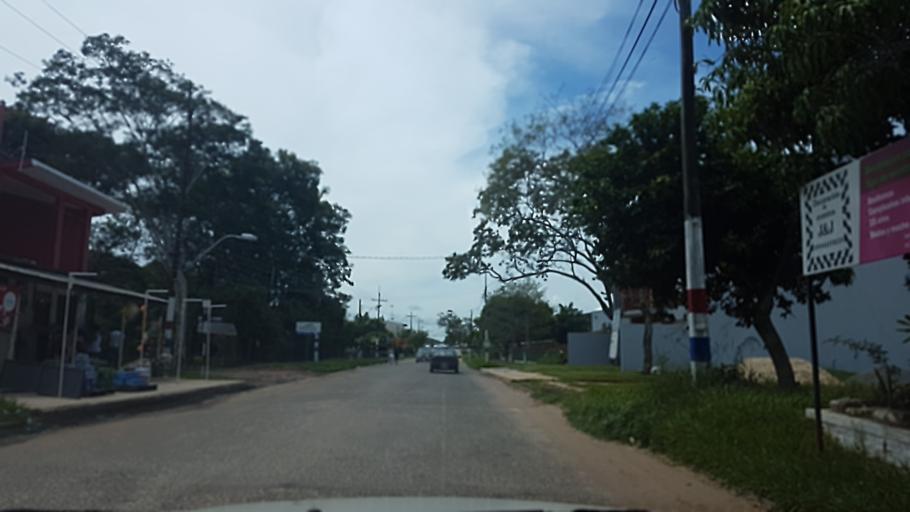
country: PY
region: Central
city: Colonia Mariano Roque Alonso
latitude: -25.1965
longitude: -57.5351
